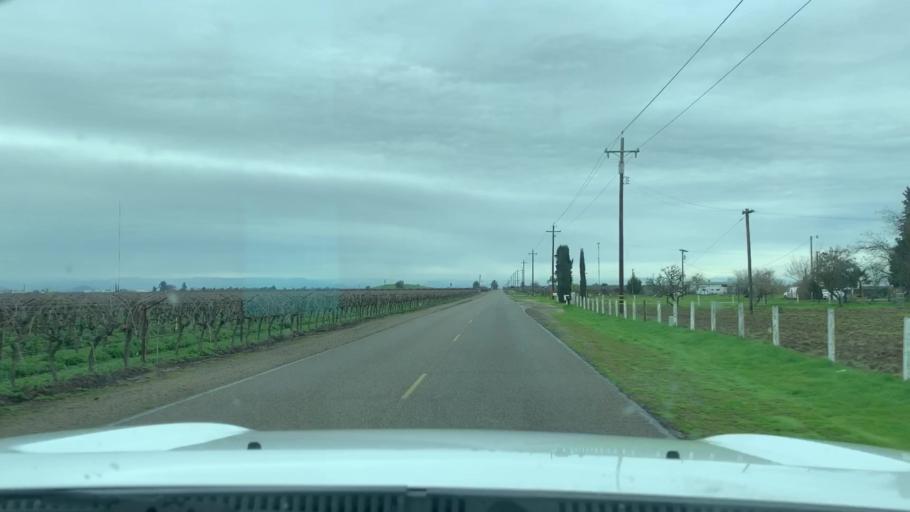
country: US
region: California
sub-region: Fresno County
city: Caruthers
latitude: 36.5474
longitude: -119.7682
